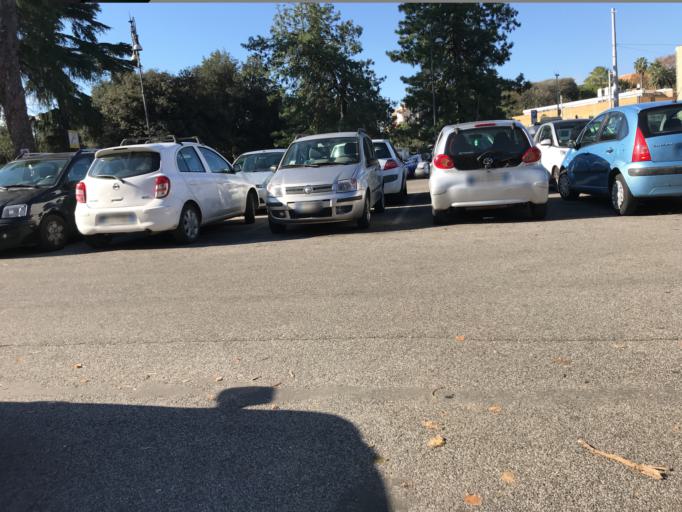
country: IT
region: Latium
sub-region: Citta metropolitana di Roma Capitale
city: Rome
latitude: 41.9022
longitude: 12.5201
